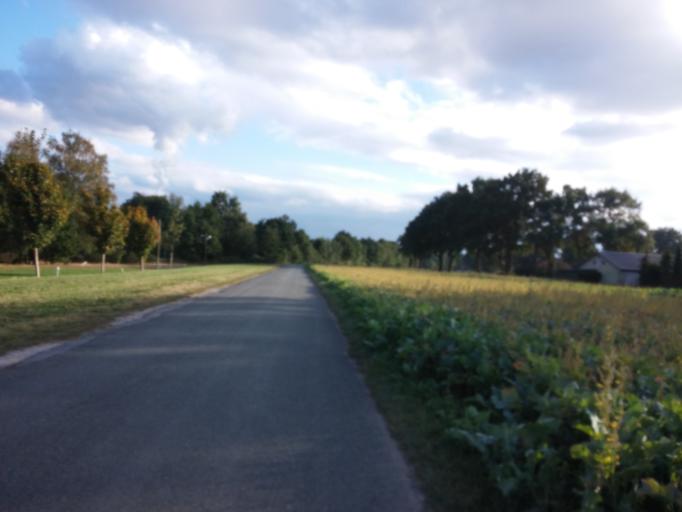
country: DE
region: North Rhine-Westphalia
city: Dorsten
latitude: 51.6438
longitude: 6.9688
